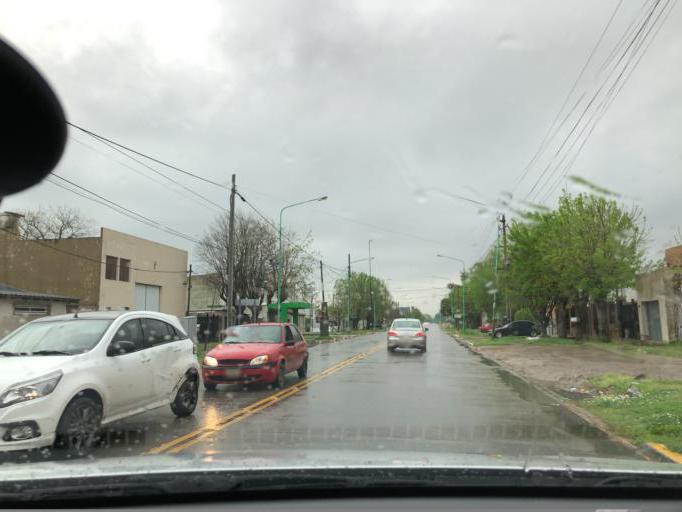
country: AR
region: Buenos Aires
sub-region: Partido de Ensenada
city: Ensenada
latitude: -34.8520
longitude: -57.9230
